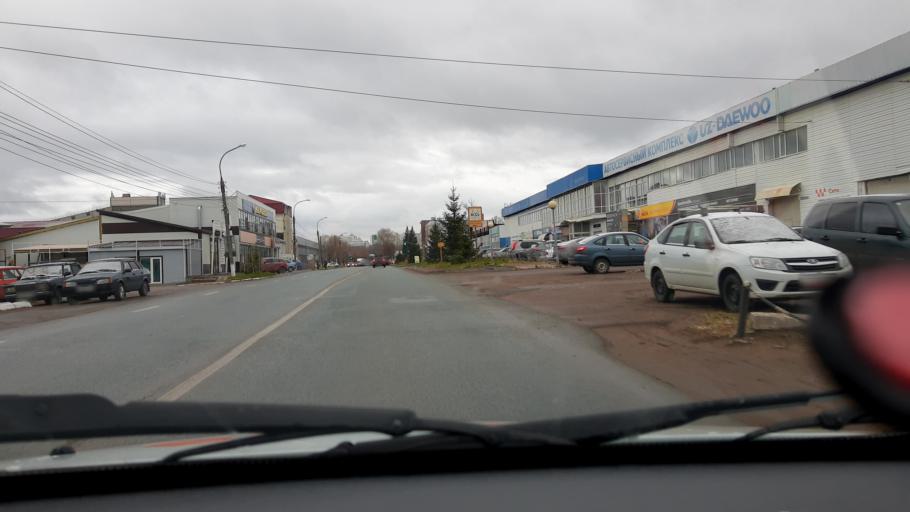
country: RU
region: Bashkortostan
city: Ufa
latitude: 54.8059
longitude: 56.0880
